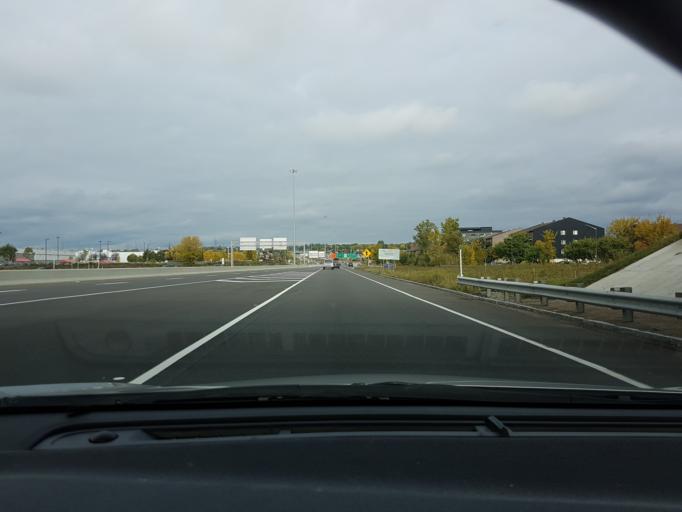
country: CA
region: Quebec
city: Quebec
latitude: 46.8391
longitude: -71.2656
